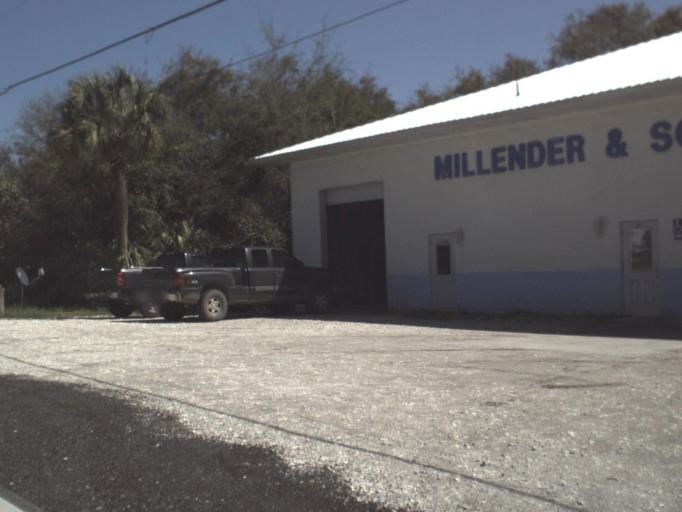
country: US
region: Florida
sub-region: Franklin County
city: Carrabelle
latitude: 29.8502
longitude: -84.6596
